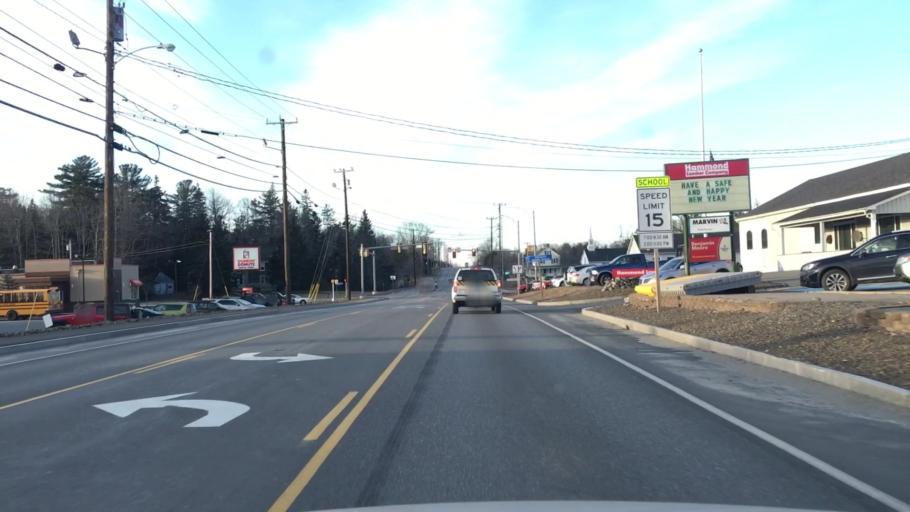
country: US
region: Maine
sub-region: Hancock County
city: Ellsworth
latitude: 44.5520
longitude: -68.4287
